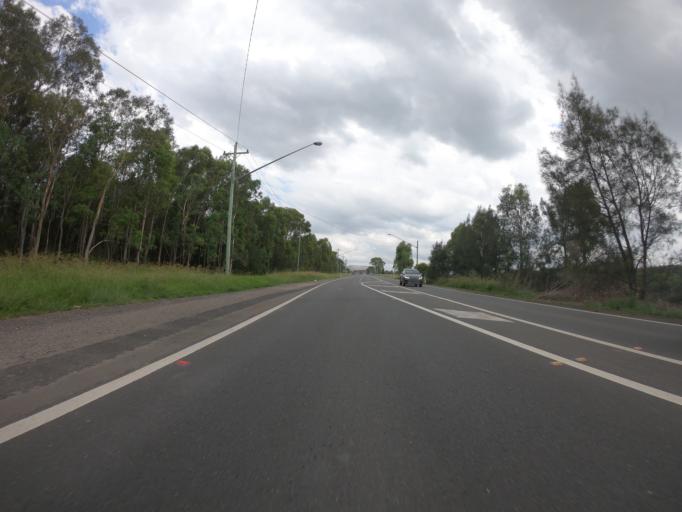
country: AU
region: New South Wales
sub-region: Blacktown
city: Mount Druitt
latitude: -33.8145
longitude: 150.7759
